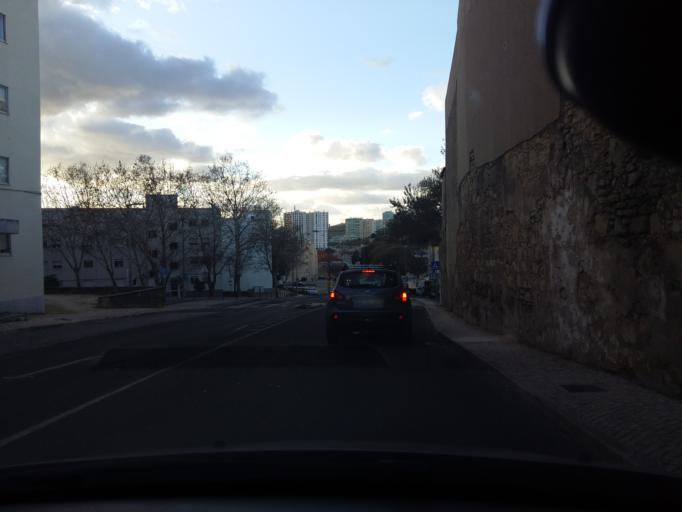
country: PT
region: Lisbon
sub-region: Odivelas
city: Pontinha
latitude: 38.7596
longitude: -9.1901
